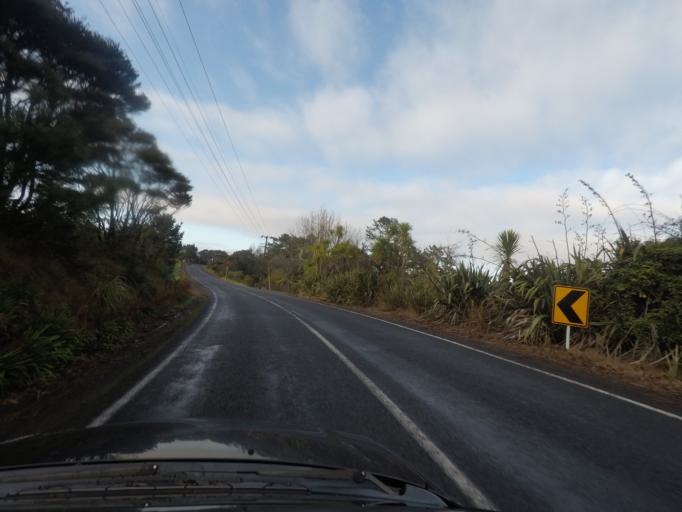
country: NZ
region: Auckland
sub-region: Auckland
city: Waitakere
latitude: -36.9076
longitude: 174.6081
